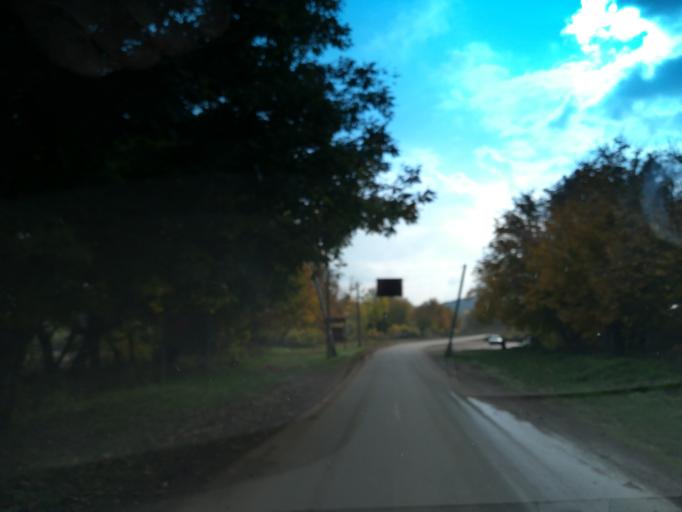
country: BG
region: Stara Zagora
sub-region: Obshtina Nikolaevo
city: Elkhovo
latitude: 42.3391
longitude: 25.4055
